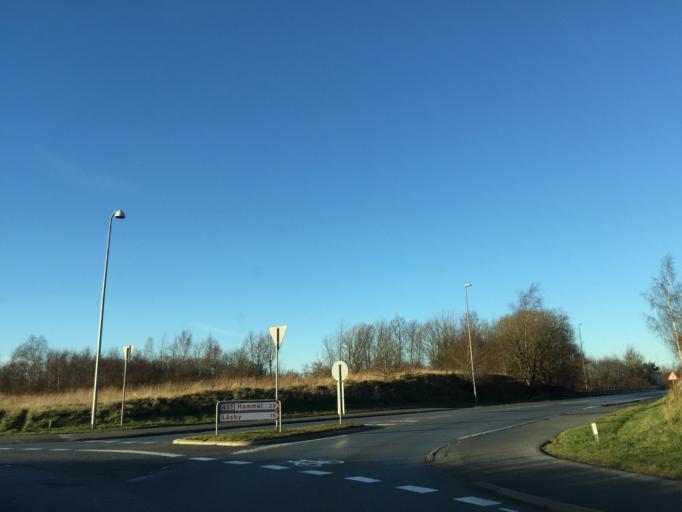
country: DK
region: Central Jutland
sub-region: Skanderborg Kommune
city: Skanderborg
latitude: 56.0476
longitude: 9.9200
